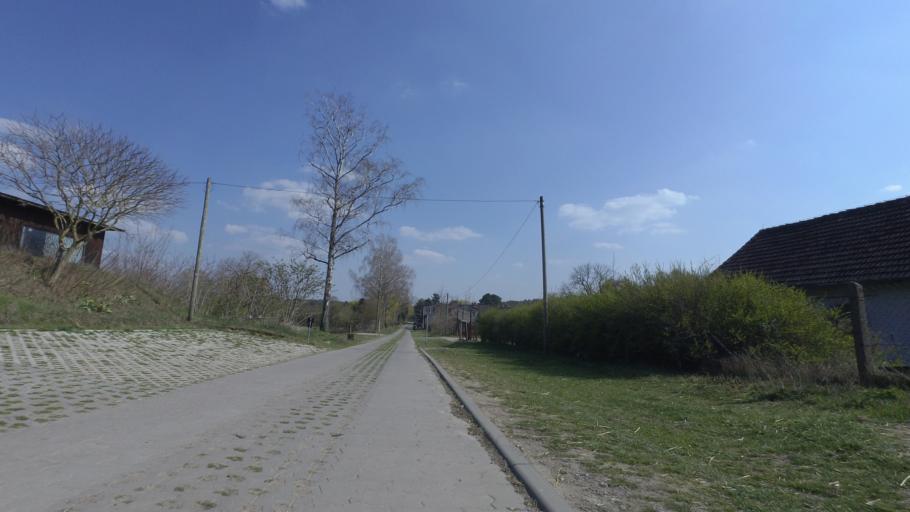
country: DE
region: Brandenburg
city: Teupitz
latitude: 52.1785
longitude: 13.5628
